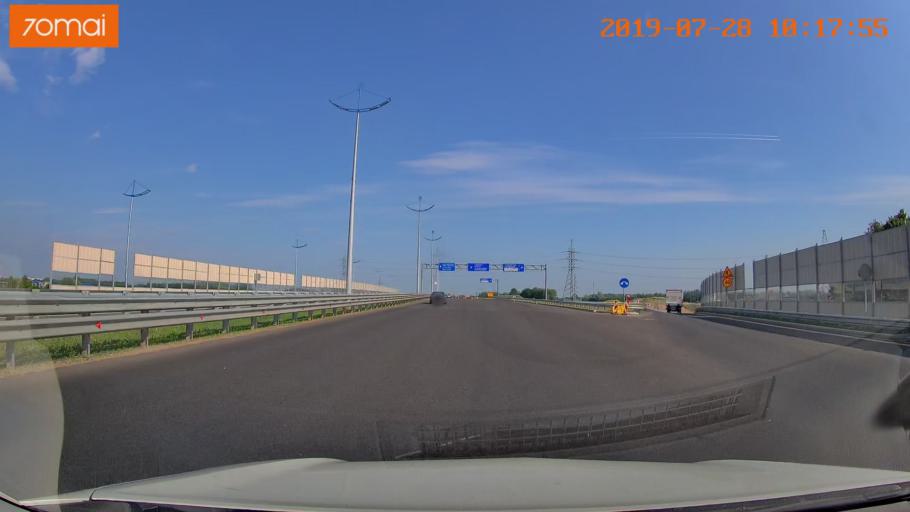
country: RU
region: Kaliningrad
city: Maloye Isakovo
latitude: 54.7454
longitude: 20.5919
